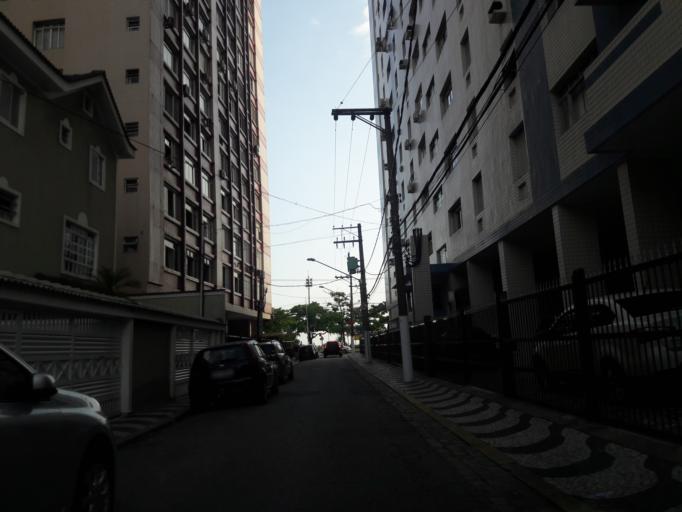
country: BR
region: Sao Paulo
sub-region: Santos
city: Santos
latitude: -23.9675
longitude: -46.3405
